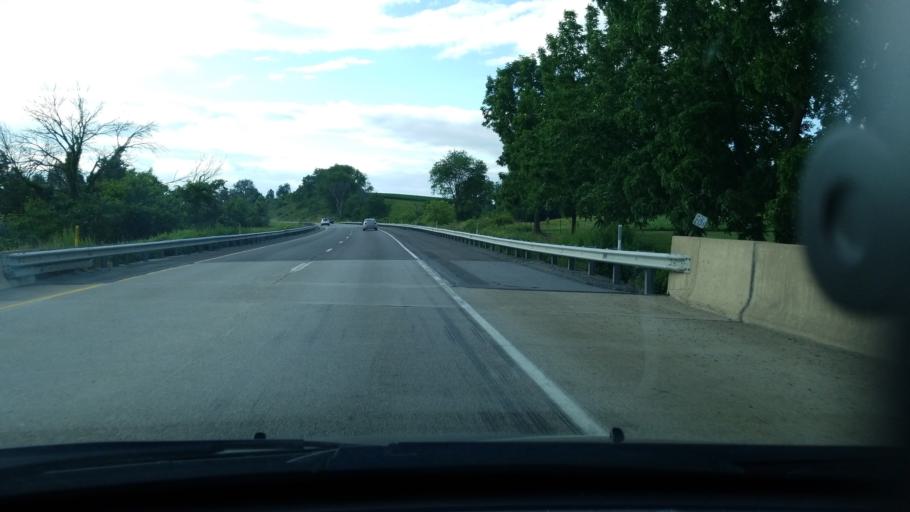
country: US
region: Pennsylvania
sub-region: Northumberland County
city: Milton
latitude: 41.0395
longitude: -76.8109
